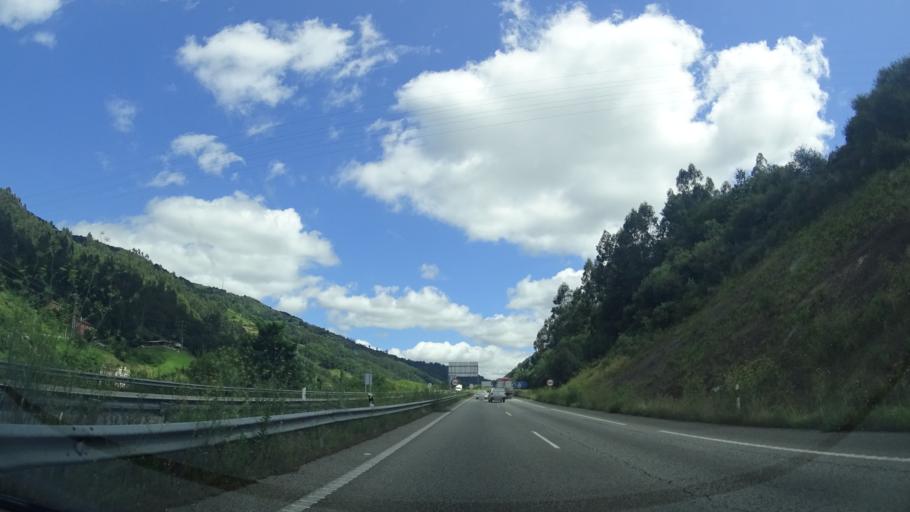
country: ES
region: Asturias
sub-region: Province of Asturias
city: Mieres
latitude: 43.2647
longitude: -5.7783
